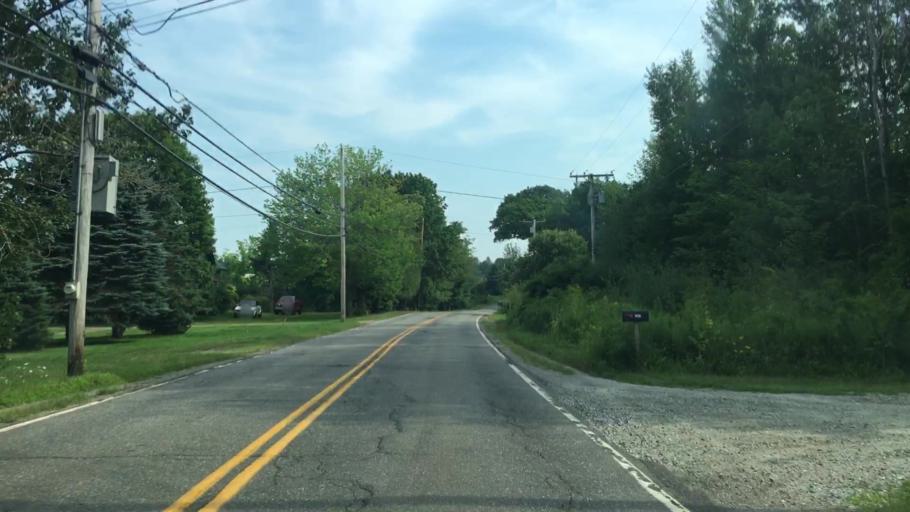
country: US
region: Maine
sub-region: Knox County
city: Friendship
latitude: 44.0386
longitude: -69.3296
